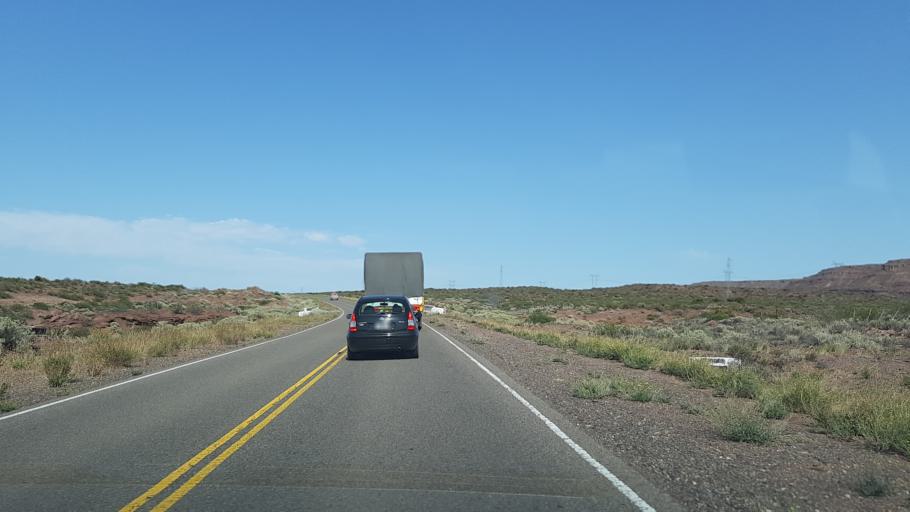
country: AR
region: Neuquen
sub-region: Departamento de Picun Leufu
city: Picun Leufu
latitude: -39.2958
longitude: -68.8974
